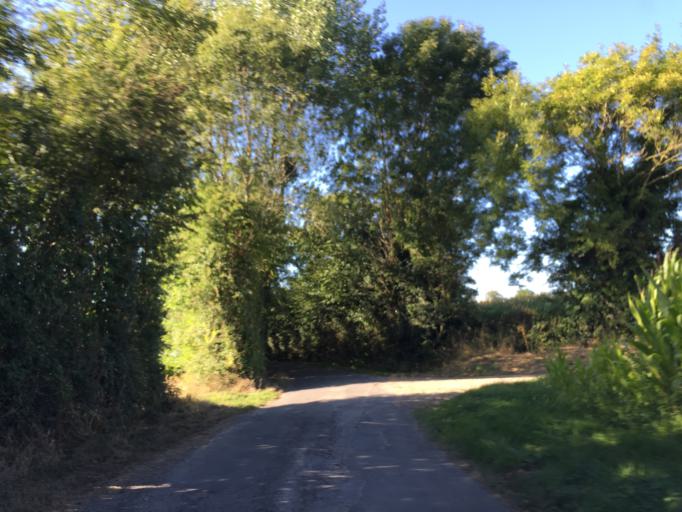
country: FR
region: Lower Normandy
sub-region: Departement du Calvados
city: Equemauville
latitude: 49.4038
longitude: 0.1948
